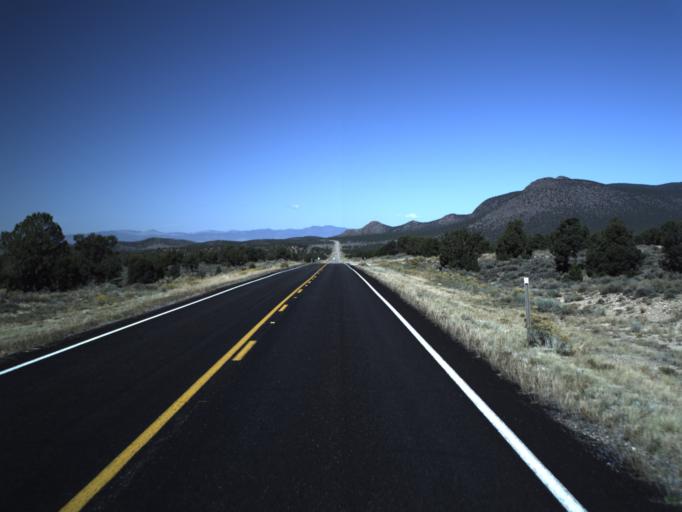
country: US
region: Utah
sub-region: Washington County
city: Enterprise
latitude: 37.6280
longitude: -113.4234
